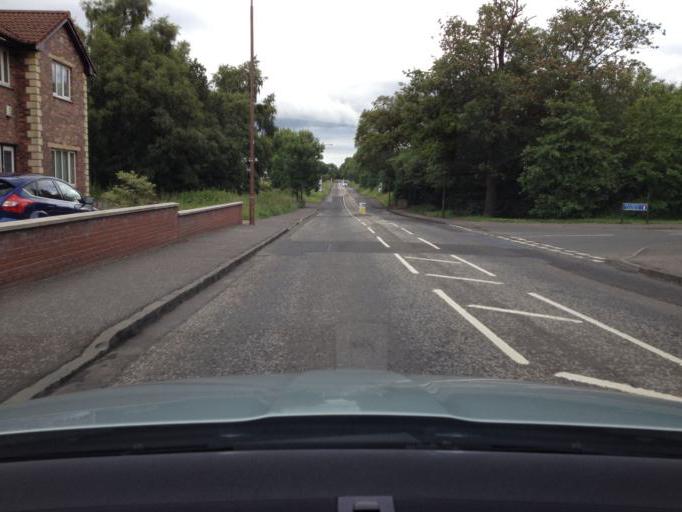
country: GB
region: Scotland
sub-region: West Lothian
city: West Calder
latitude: 55.8800
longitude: -3.5862
